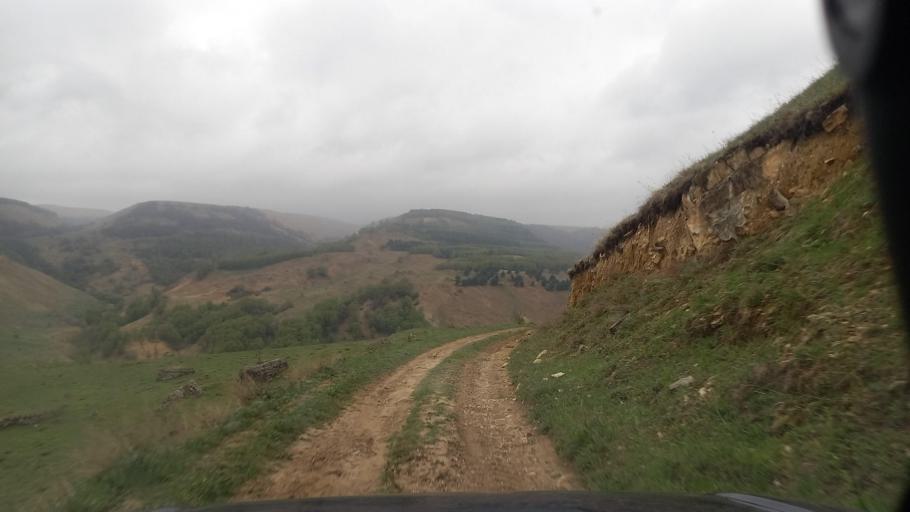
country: RU
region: Stavropol'skiy
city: Nezhinskiy
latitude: 43.8516
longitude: 42.6385
